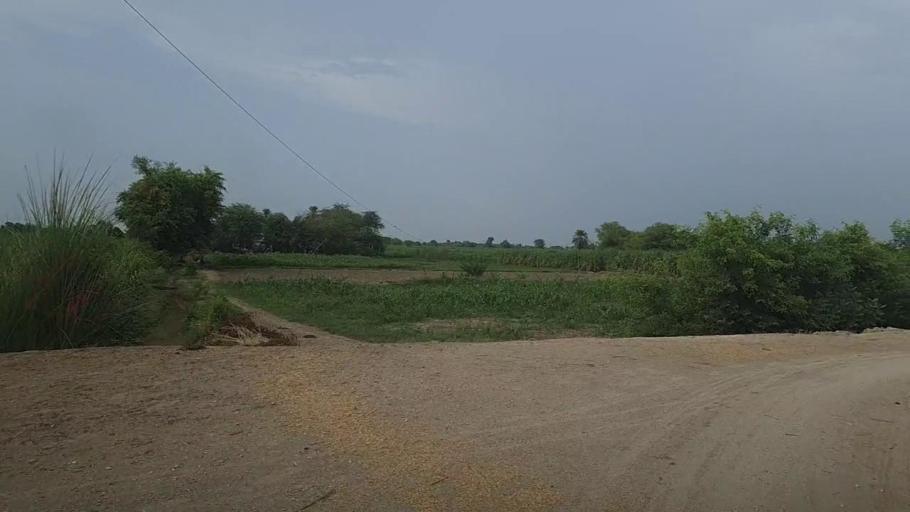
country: PK
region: Sindh
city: Karaundi
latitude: 26.9768
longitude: 68.4289
